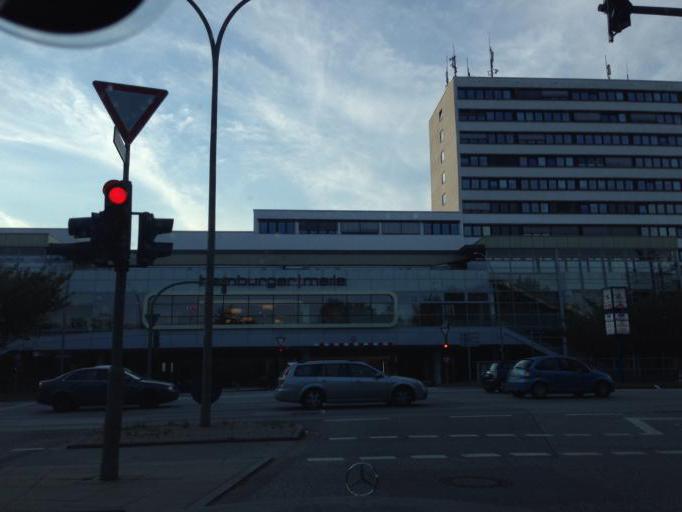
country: DE
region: Hamburg
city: Hamburg
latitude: 53.5735
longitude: 10.0339
